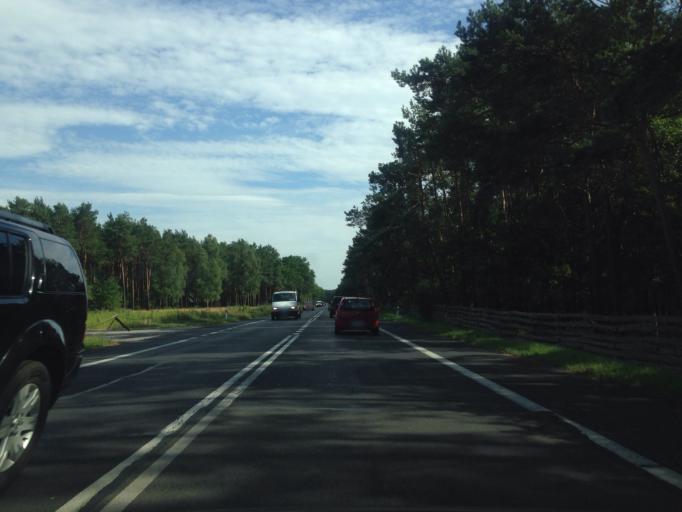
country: PL
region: Kujawsko-Pomorskie
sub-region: Powiat aleksandrowski
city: Aleksandrow Kujawski
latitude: 52.8937
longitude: 18.7299
